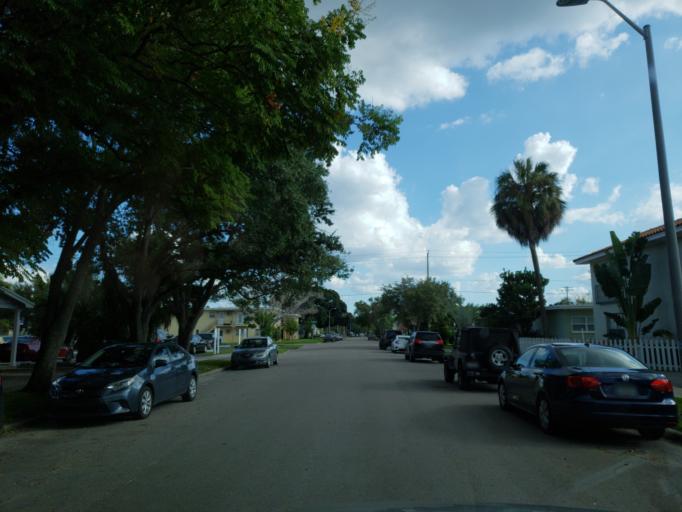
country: US
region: Florida
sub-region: Hillsborough County
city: Tampa
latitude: 27.9265
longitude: -82.4543
